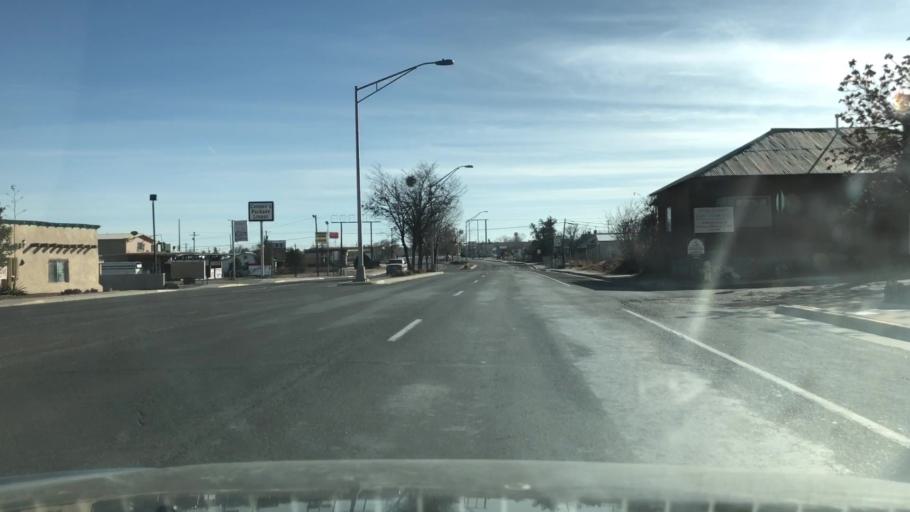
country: US
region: New Mexico
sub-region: Socorro County
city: Socorro
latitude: 34.0561
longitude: -106.8916
